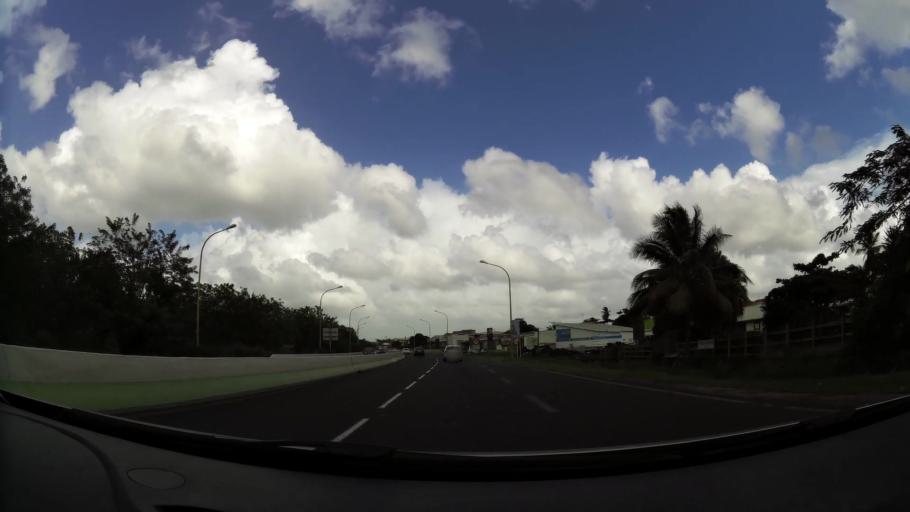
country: MQ
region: Martinique
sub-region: Martinique
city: Ducos
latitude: 14.5264
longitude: -60.9821
